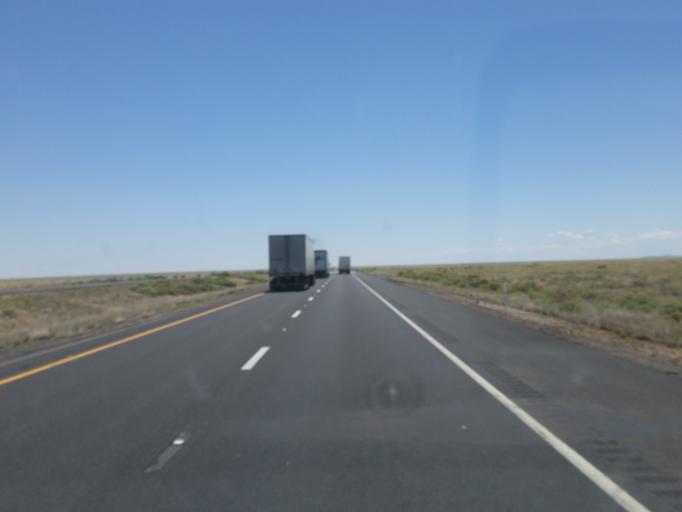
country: US
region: Arizona
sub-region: Coconino County
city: Flagstaff
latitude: 35.1488
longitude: -111.2380
